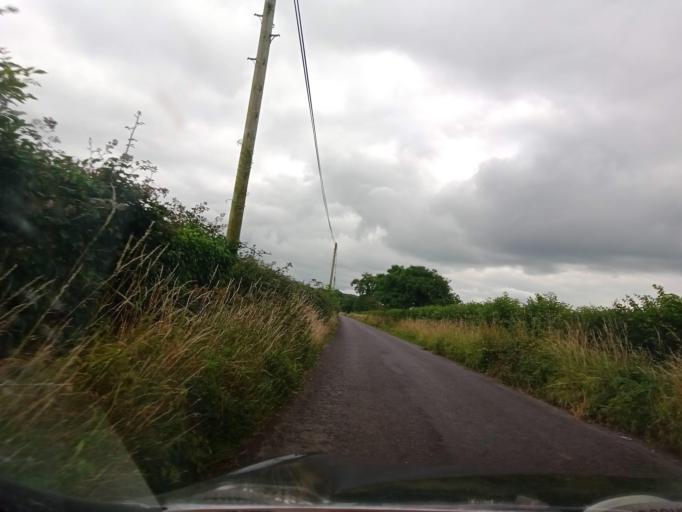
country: IE
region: Leinster
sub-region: Laois
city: Stradbally
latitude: 52.9863
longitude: -7.1740
